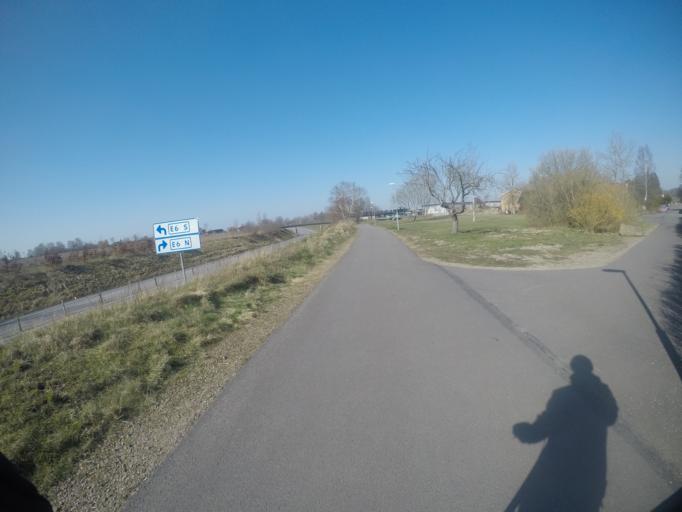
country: SE
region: Halland
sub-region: Laholms Kommun
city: Laholm
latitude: 56.5005
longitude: 13.0410
